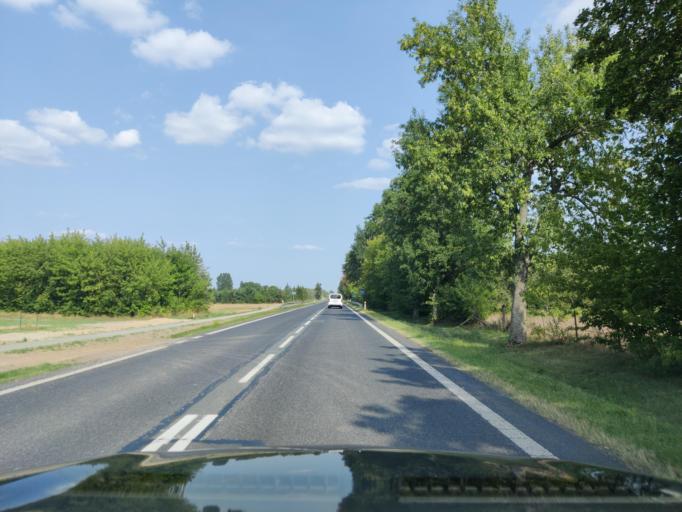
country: PL
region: Masovian Voivodeship
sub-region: Powiat makowski
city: Rozan
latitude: 52.8797
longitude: 21.3693
